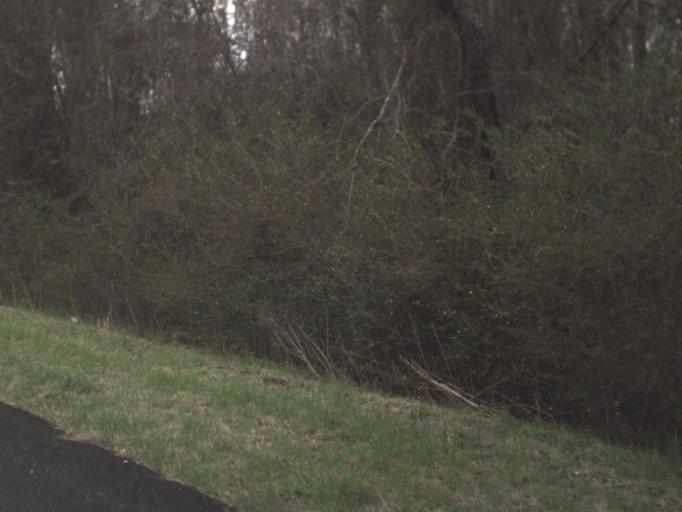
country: US
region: Florida
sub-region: Jefferson County
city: Monticello
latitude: 30.3814
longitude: -83.8221
